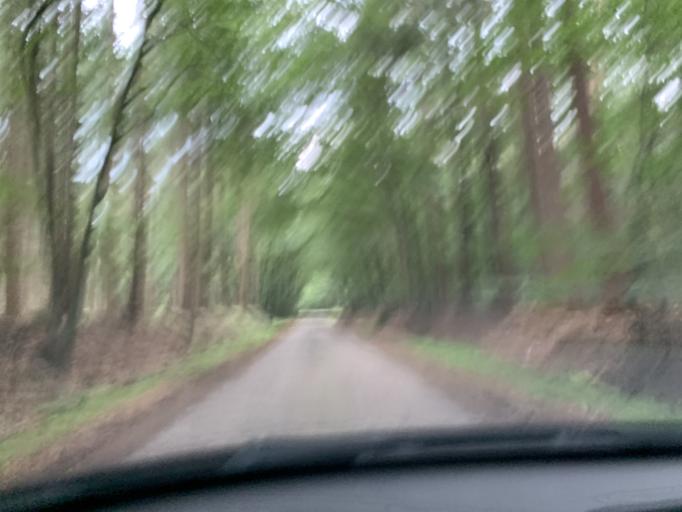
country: DE
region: Lower Saxony
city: Westerstede
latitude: 53.2685
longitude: 7.9955
